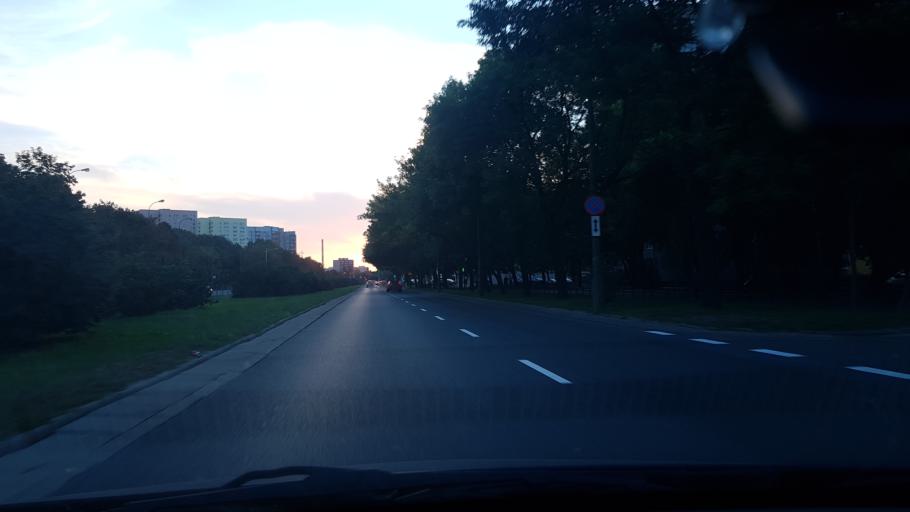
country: PL
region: Masovian Voivodeship
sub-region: Warszawa
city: Targowek
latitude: 52.2927
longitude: 21.0402
